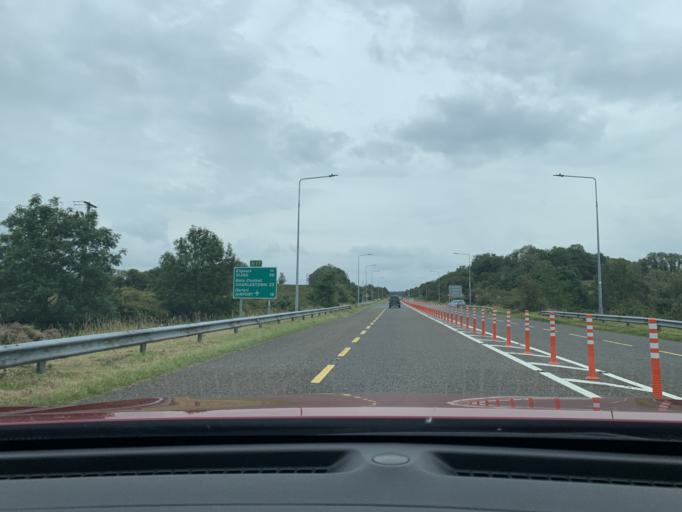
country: IE
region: Connaught
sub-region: Maigh Eo
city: Kiltamagh
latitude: 53.7997
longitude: -8.9203
